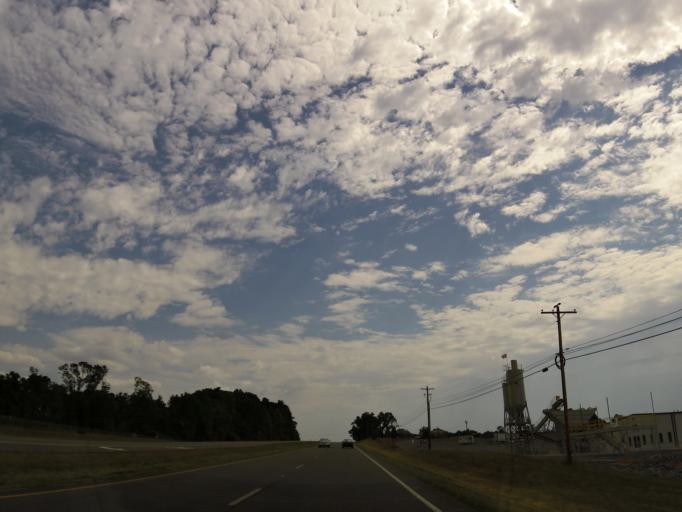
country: US
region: Alabama
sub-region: Jackson County
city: Stevenson
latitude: 34.8289
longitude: -85.8389
